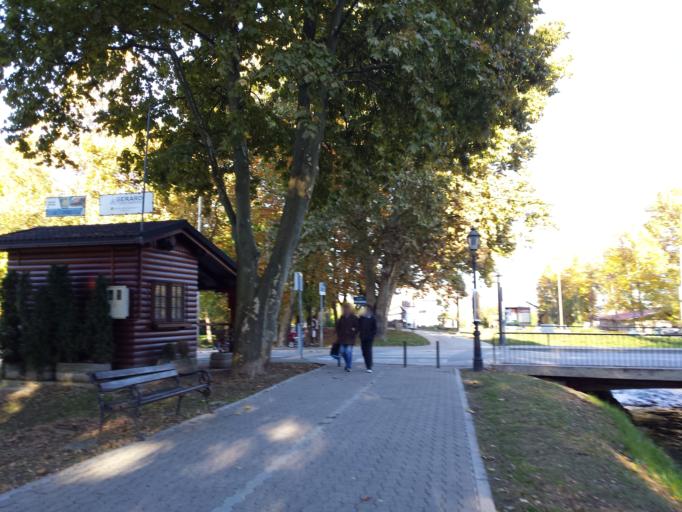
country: HR
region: Zagrebacka
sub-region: Grad Samobor
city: Samobor
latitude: 45.8030
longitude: 15.7140
